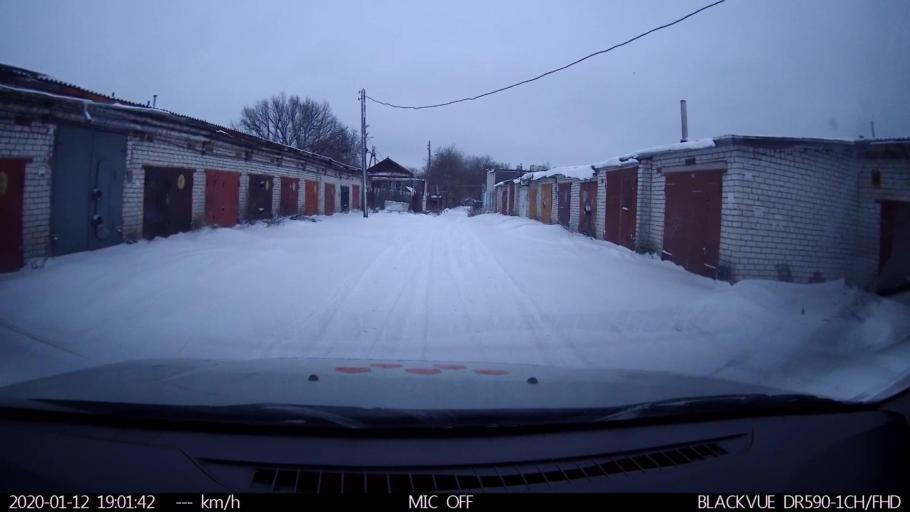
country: RU
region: Nizjnij Novgorod
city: Nizhniy Novgorod
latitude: 56.3325
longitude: 43.9081
